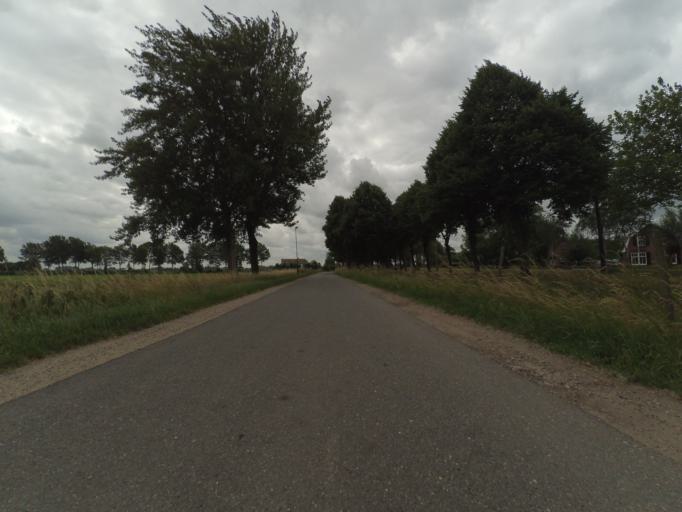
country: NL
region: South Holland
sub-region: Gemeente Gorinchem
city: Gorinchem
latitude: 51.8745
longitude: 5.0060
